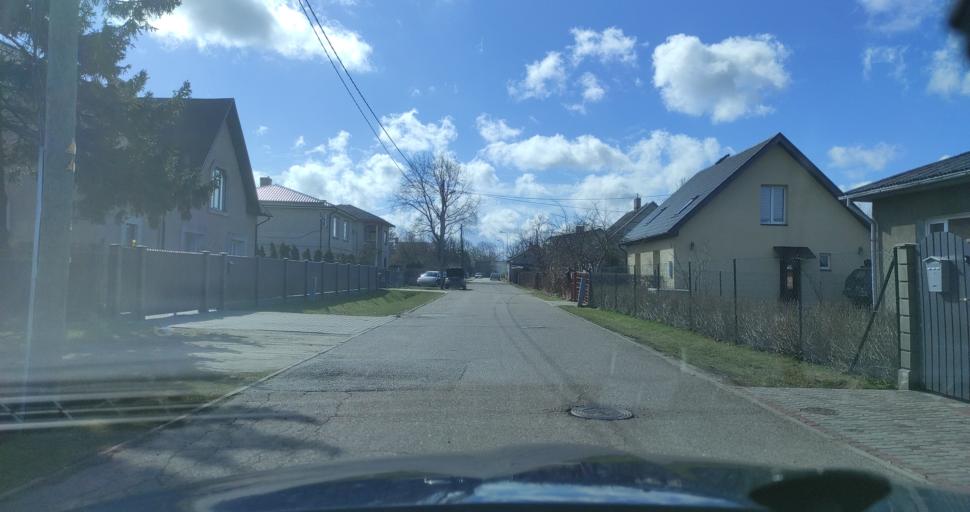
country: LV
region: Ventspils
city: Ventspils
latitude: 57.3773
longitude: 21.5708
